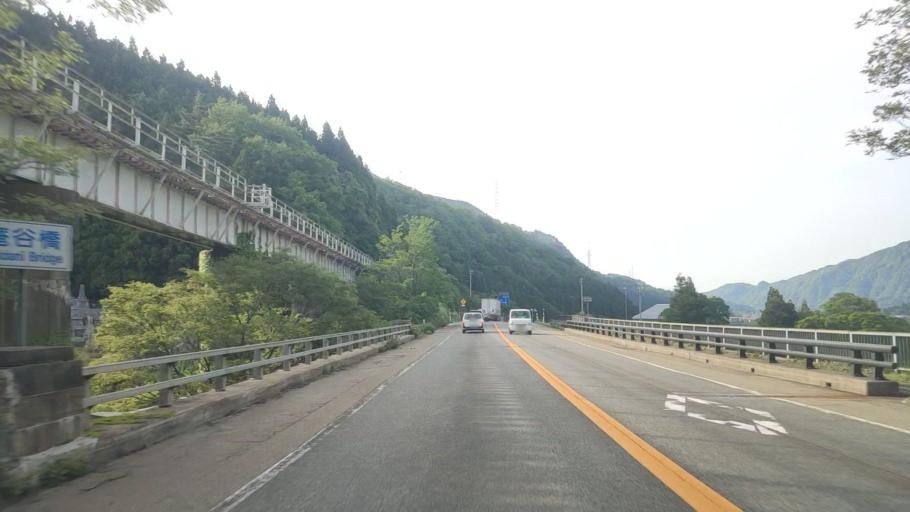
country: JP
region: Toyama
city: Yatsuomachi-higashikumisaka
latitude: 36.5089
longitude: 137.2289
